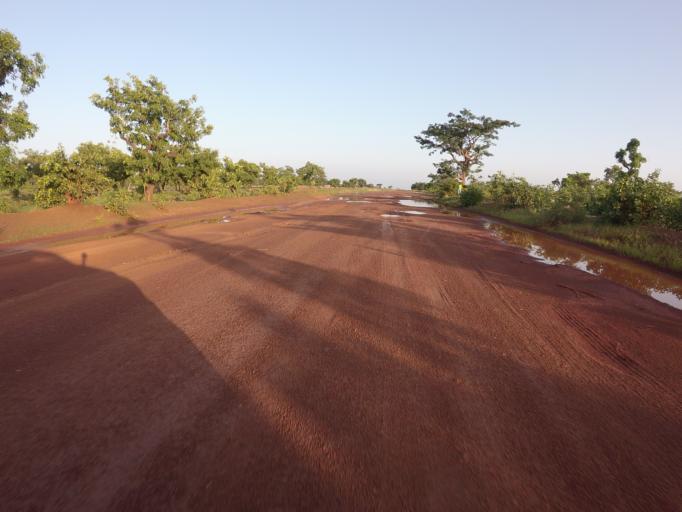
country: TG
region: Savanes
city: Sansanne-Mango
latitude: 10.2337
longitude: -0.0734
